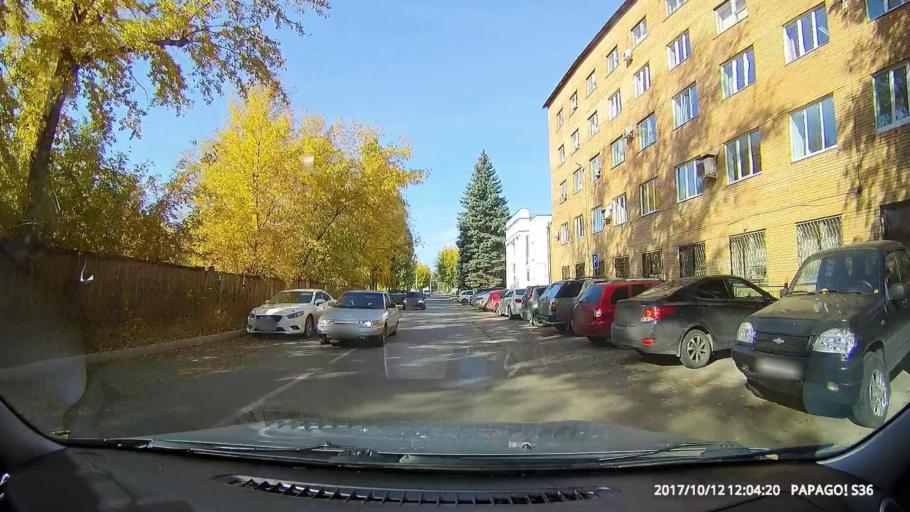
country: RU
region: Samara
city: Chapayevsk
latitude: 52.9777
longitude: 49.7169
